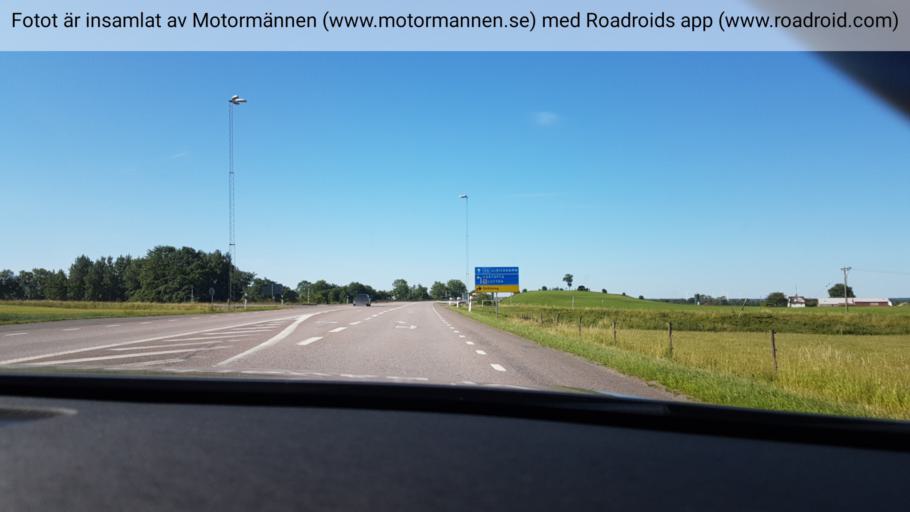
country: SE
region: Vaestra Goetaland
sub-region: Falkopings Kommun
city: Falkoeping
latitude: 58.1357
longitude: 13.5626
